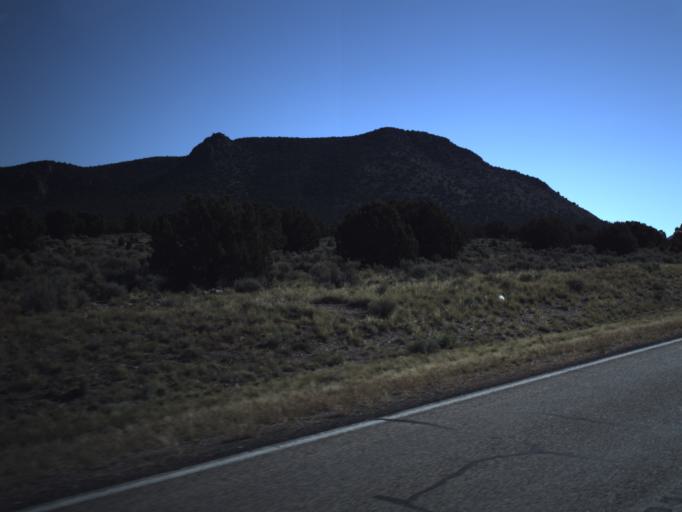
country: US
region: Utah
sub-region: Washington County
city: Enterprise
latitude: 37.6658
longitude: -113.4747
